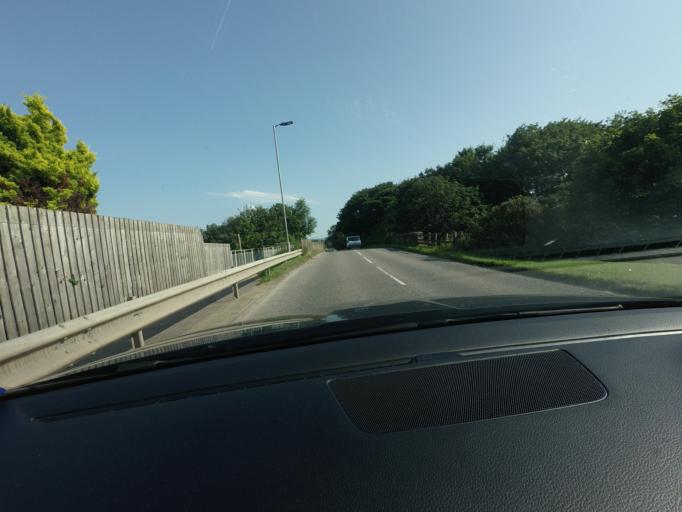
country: GB
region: Scotland
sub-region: Highland
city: Alness
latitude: 57.6941
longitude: -4.2450
